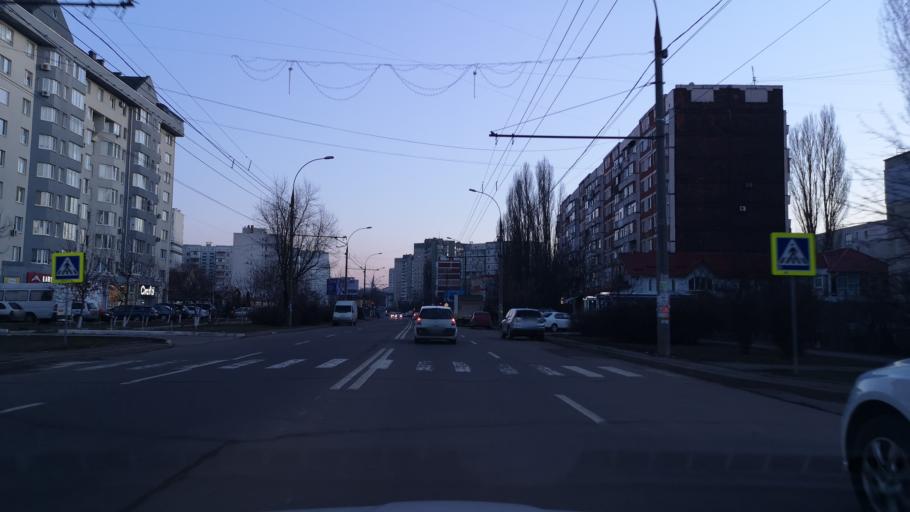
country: MD
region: Chisinau
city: Stauceni
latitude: 47.0595
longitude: 28.8469
